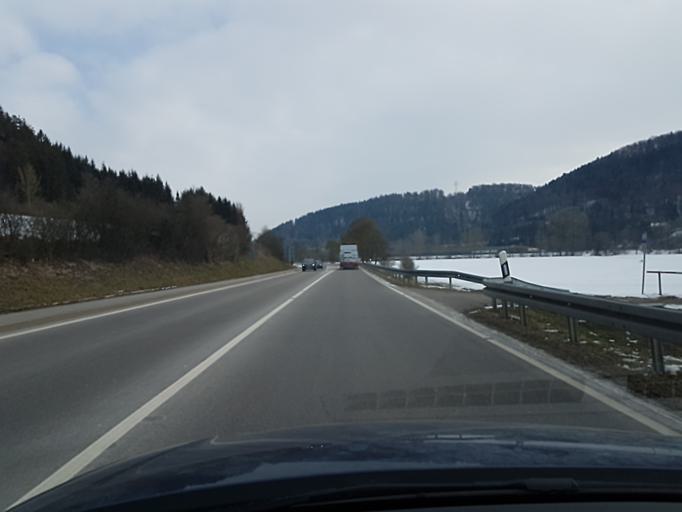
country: DE
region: Baden-Wuerttemberg
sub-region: Karlsruhe Region
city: Horb am Neckar
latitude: 48.4345
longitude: 8.6660
